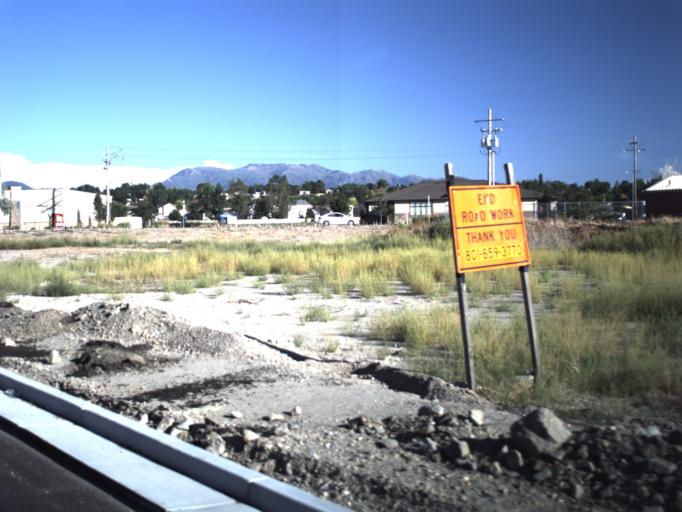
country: US
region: Utah
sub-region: Weber County
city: West Haven
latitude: 41.1905
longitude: -112.0500
